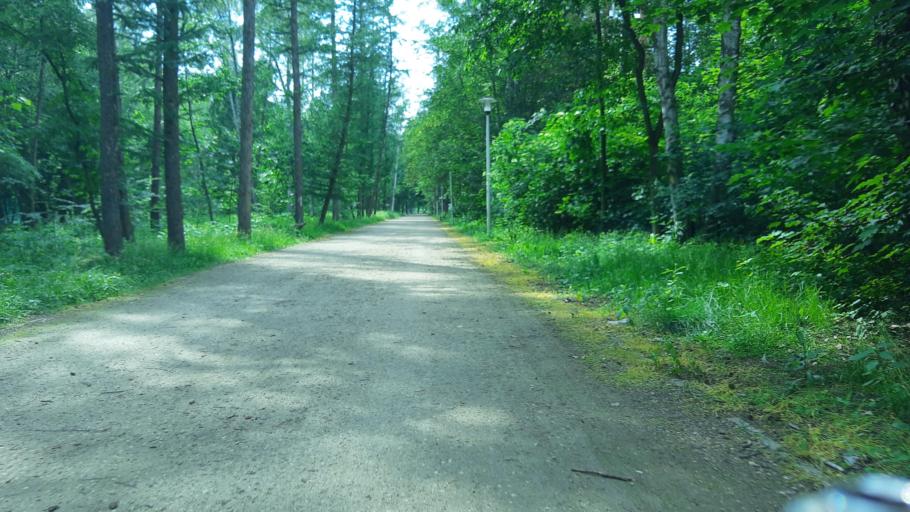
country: PL
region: Lodz Voivodeship
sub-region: Powiat sieradzki
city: Sieradz
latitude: 51.5966
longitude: 18.7580
